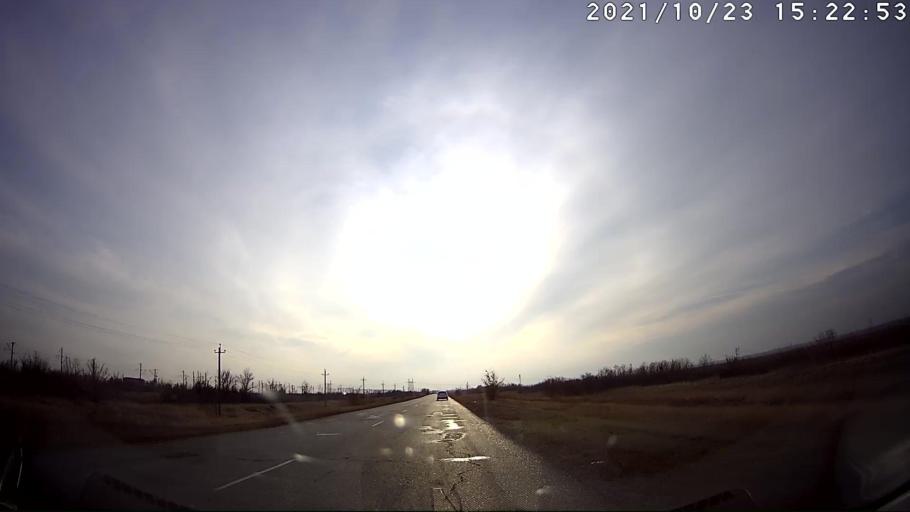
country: RU
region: Volgograd
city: Bereslavka
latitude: 48.3020
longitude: 44.2938
